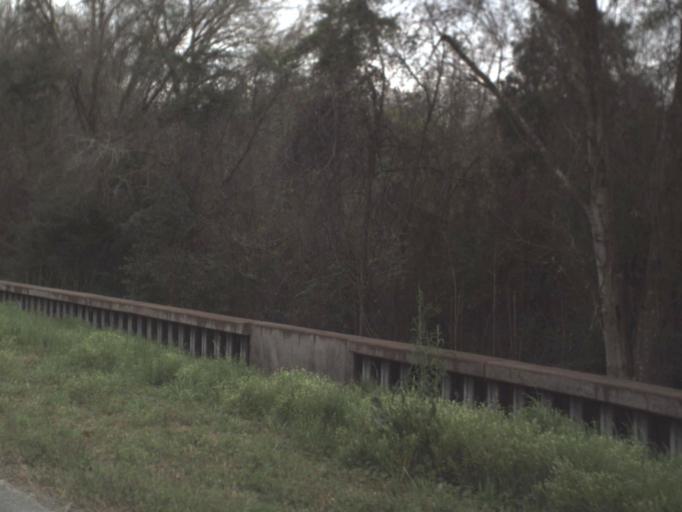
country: US
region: Florida
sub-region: Gadsden County
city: Midway
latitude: 30.5273
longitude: -84.3574
